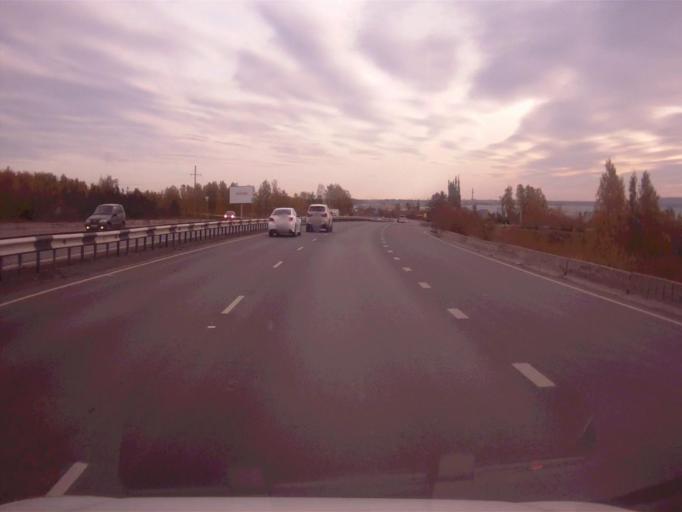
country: RU
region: Chelyabinsk
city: Novosineglazovskiy
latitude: 55.0386
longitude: 61.4409
